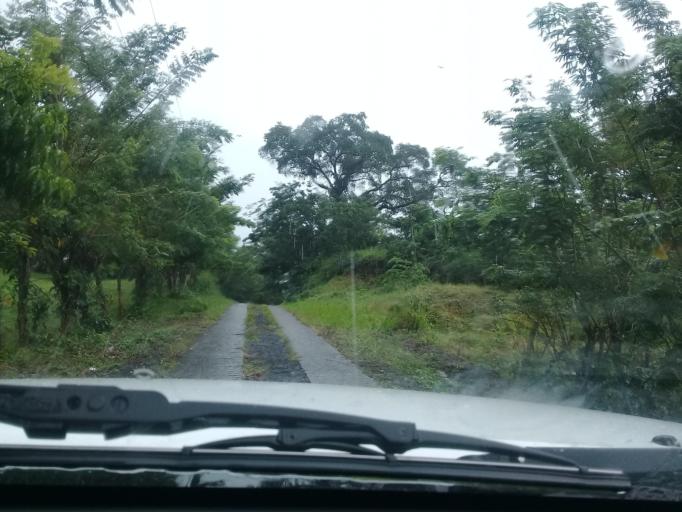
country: MX
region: Veracruz
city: Santiago Tuxtla
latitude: 18.4611
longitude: -95.3146
